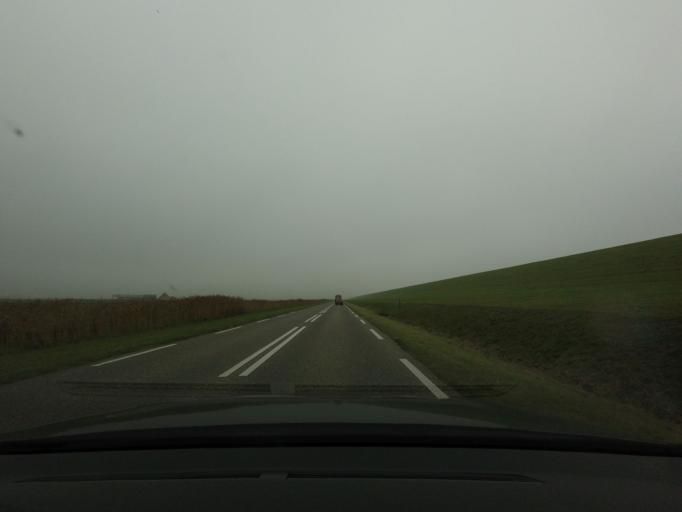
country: NL
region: North Holland
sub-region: Gemeente Bergen
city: Egmond aan Zee
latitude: 52.7451
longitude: 4.6471
